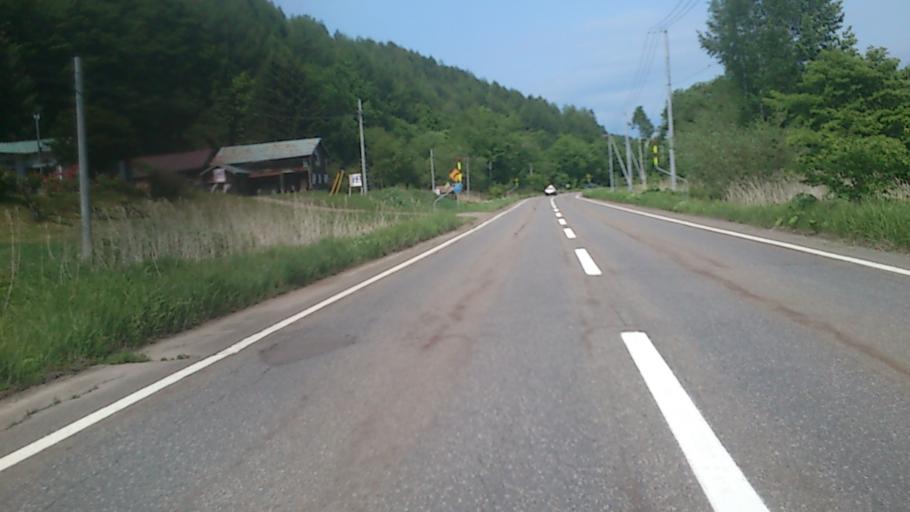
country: JP
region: Hokkaido
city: Otofuke
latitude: 43.2629
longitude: 143.5782
